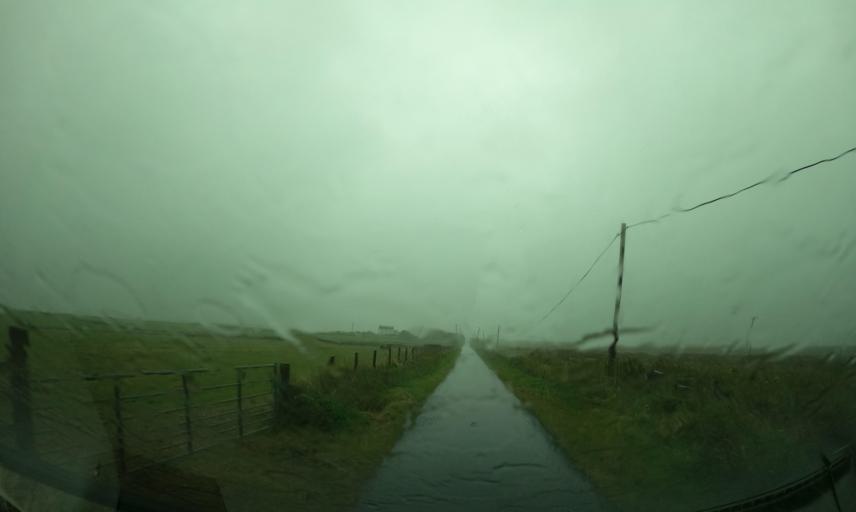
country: GB
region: Scotland
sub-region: Eilean Siar
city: Barra
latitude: 56.4637
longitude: -6.9273
